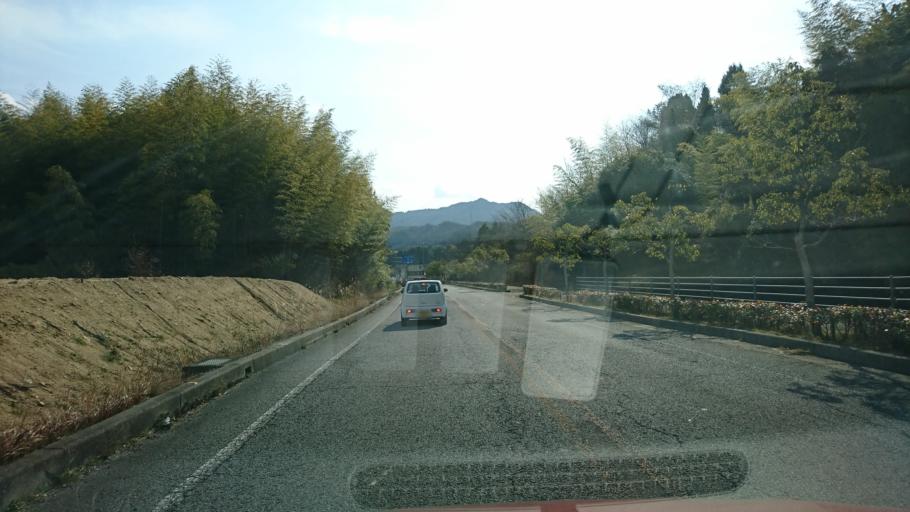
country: JP
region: Ehime
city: Saijo
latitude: 34.0075
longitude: 133.0341
